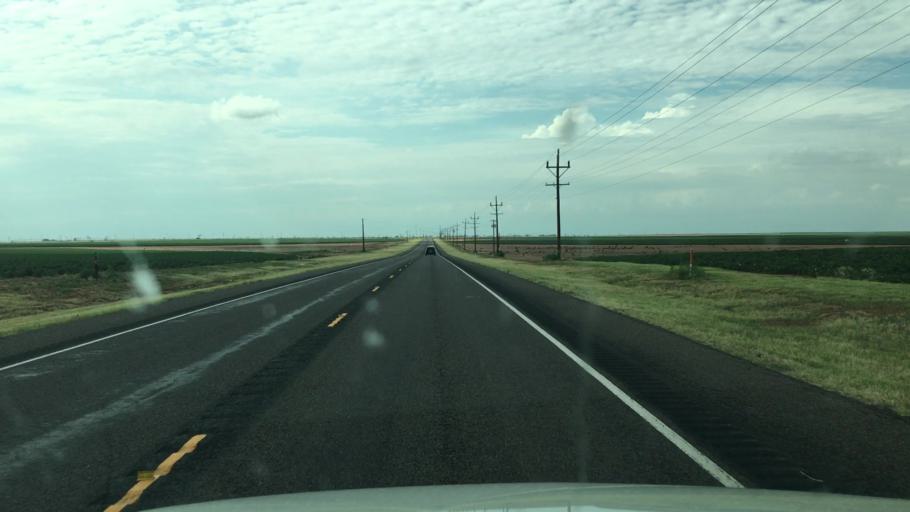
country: US
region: Texas
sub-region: Dawson County
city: Lamesa
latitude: 32.8816
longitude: -102.0815
